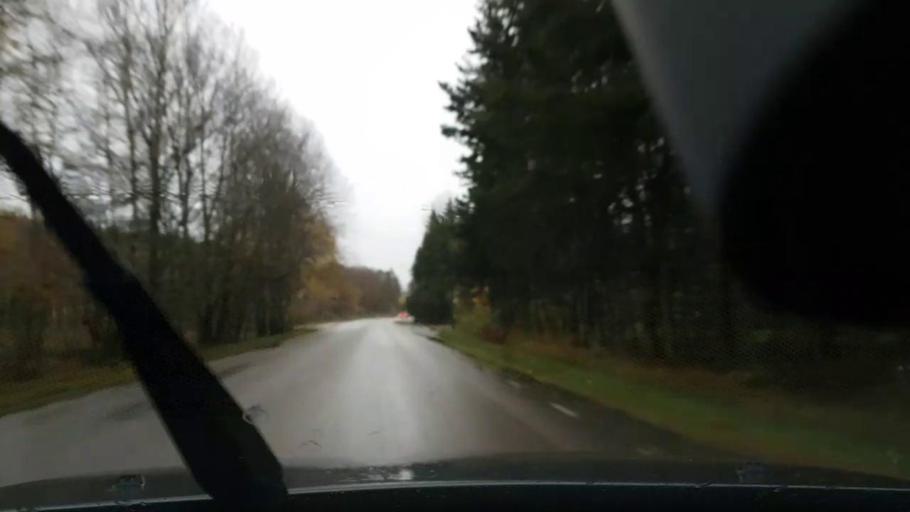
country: SE
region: Vaestra Goetaland
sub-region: Molndal
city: Lindome
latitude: 57.5935
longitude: 12.0890
